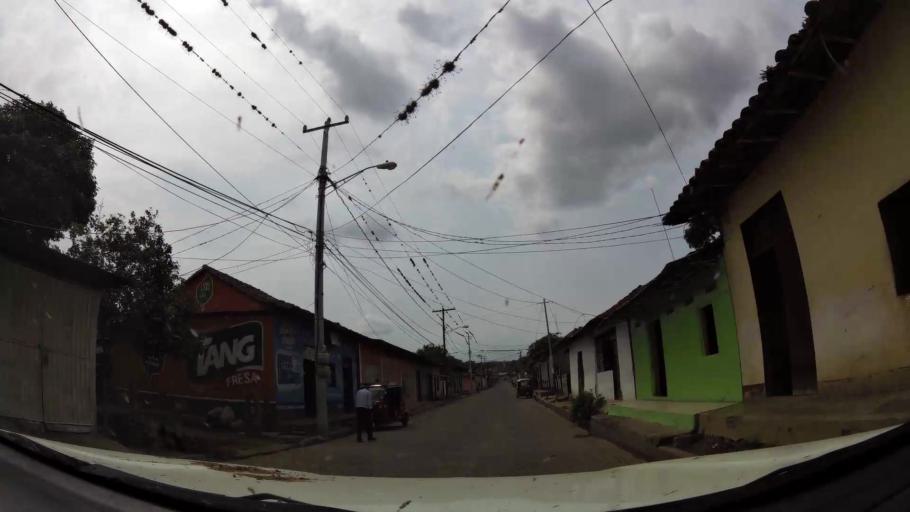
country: NI
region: Granada
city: Diria
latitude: 11.8825
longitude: -86.0542
